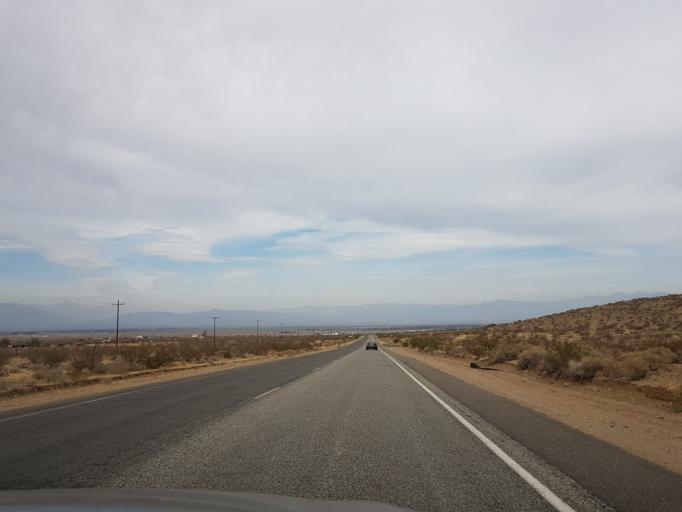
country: US
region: California
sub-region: Kern County
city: Ridgecrest
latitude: 35.5601
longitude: -117.7137
